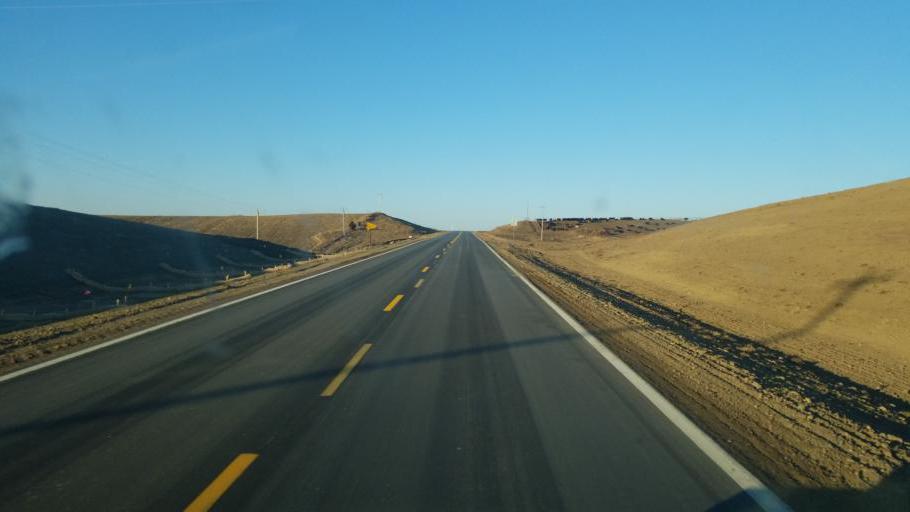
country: US
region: Nebraska
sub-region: Knox County
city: Center
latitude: 42.5971
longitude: -97.7885
